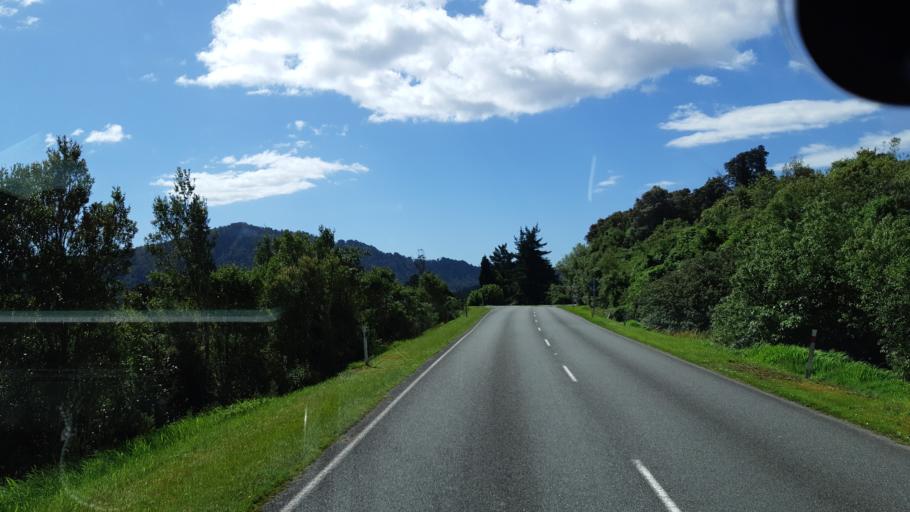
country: NZ
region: West Coast
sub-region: Westland District
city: Hokitika
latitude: -43.0874
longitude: 170.6250
